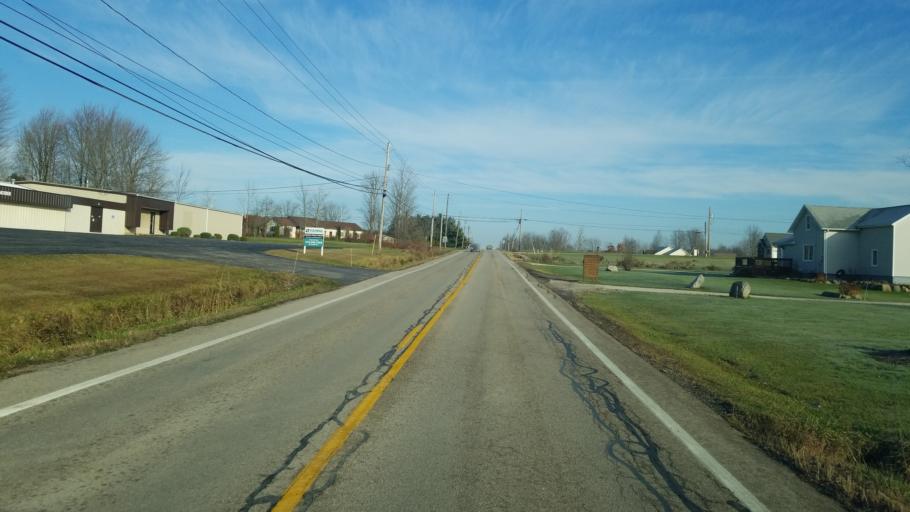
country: US
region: Ohio
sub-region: Ashtabula County
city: North Kingsville
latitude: 41.8554
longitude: -80.6662
